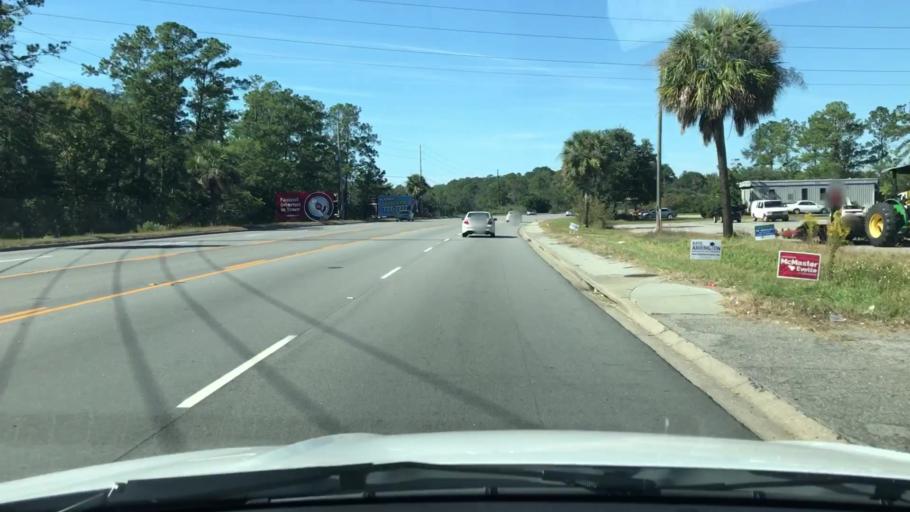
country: US
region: South Carolina
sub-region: Beaufort County
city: Burton
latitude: 32.4438
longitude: -80.7266
